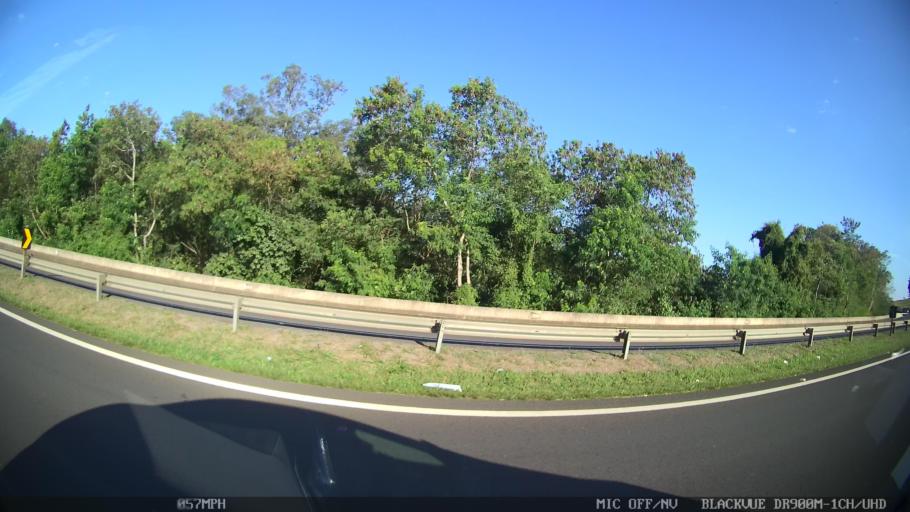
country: BR
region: Sao Paulo
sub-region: Piracicaba
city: Piracicaba
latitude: -22.6923
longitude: -47.6341
